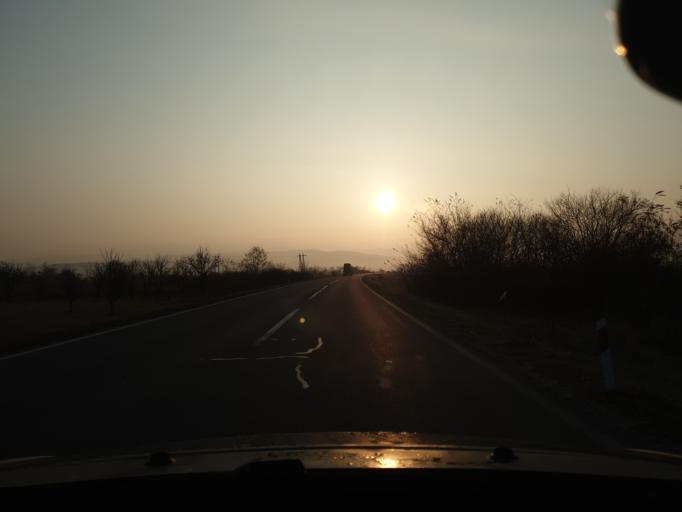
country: RS
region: Central Serbia
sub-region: Jablanicki Okrug
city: Leskovac
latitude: 42.9381
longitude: 22.0037
